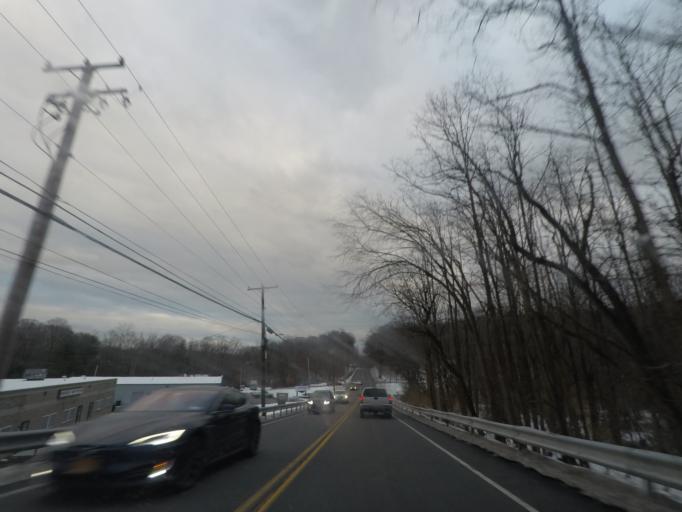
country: US
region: New York
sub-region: Orange County
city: Gardnertown
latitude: 41.5441
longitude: -74.0497
